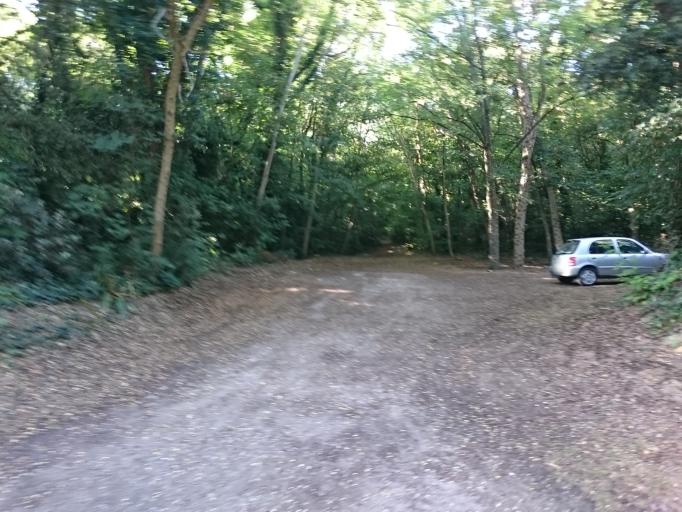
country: FR
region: Pays de la Loire
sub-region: Departement de la Vendee
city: Longeville-sur-Mer
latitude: 46.4022
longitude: -1.5043
